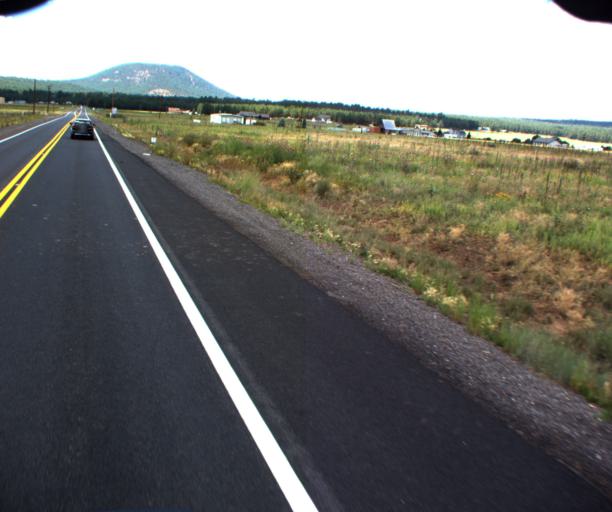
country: US
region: Arizona
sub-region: Coconino County
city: Flagstaff
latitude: 35.2684
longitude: -111.7219
